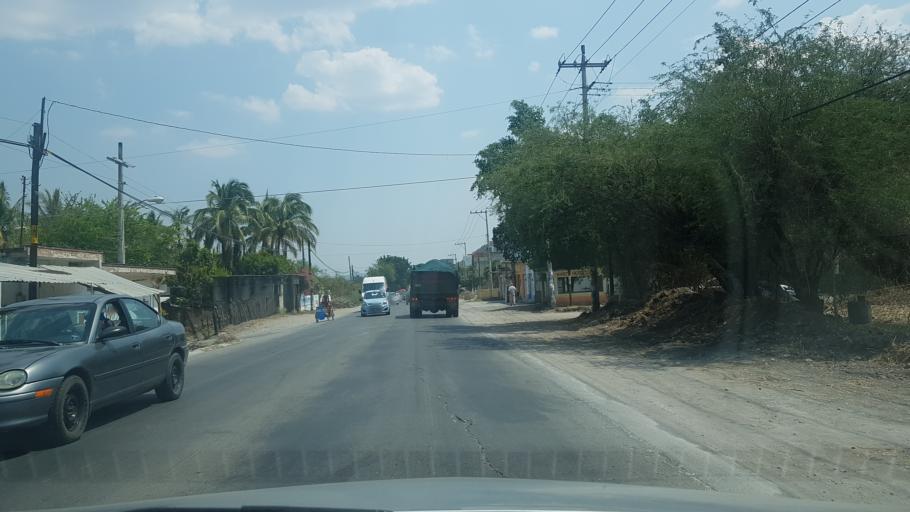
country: MX
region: Morelos
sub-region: Tlaltizapan de Zapata
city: Colonia Palo Prieto (Chipitongo)
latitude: 18.7172
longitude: -99.1197
